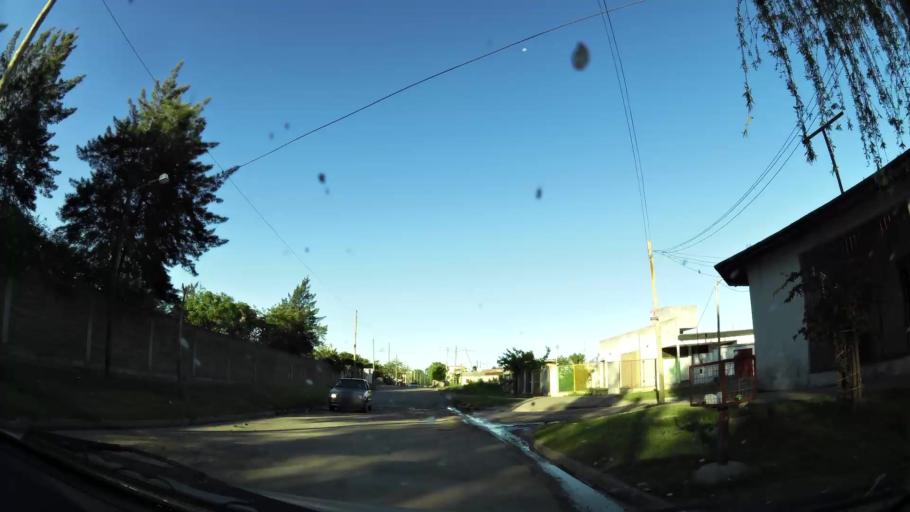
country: AR
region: Buenos Aires
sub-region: Partido de Almirante Brown
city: Adrogue
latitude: -34.7696
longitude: -58.3297
